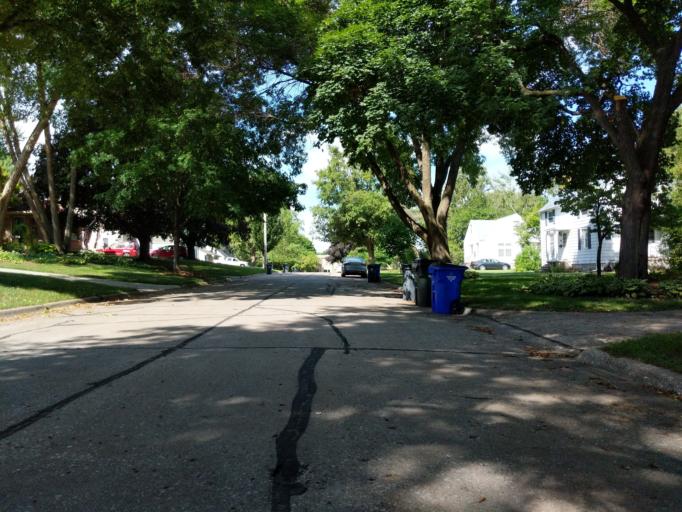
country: US
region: Iowa
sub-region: Linn County
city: Cedar Rapids
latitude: 42.0160
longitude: -91.6391
